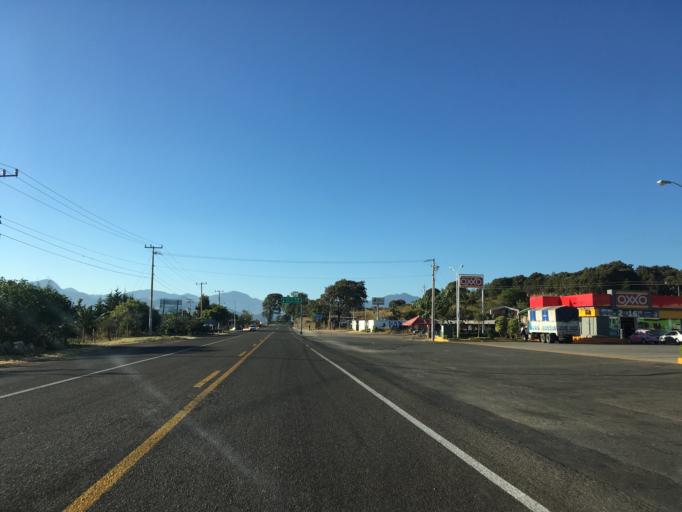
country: MX
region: Michoacan
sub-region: Zitacuaro
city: Puentecillas (Tercera Manzana de Zirahuato)
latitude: 19.4832
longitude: -100.4432
